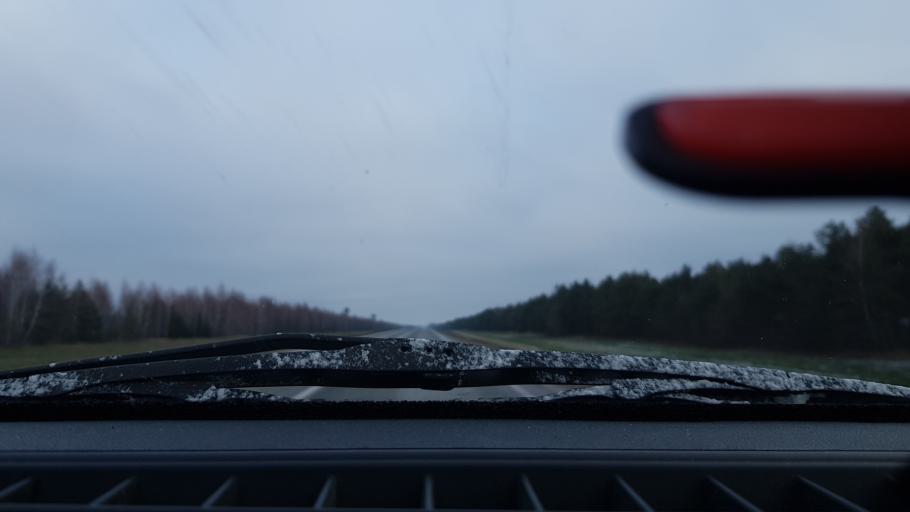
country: RU
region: Tatarstan
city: Kuybyshevskiy Zaton
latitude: 54.9552
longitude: 49.4754
